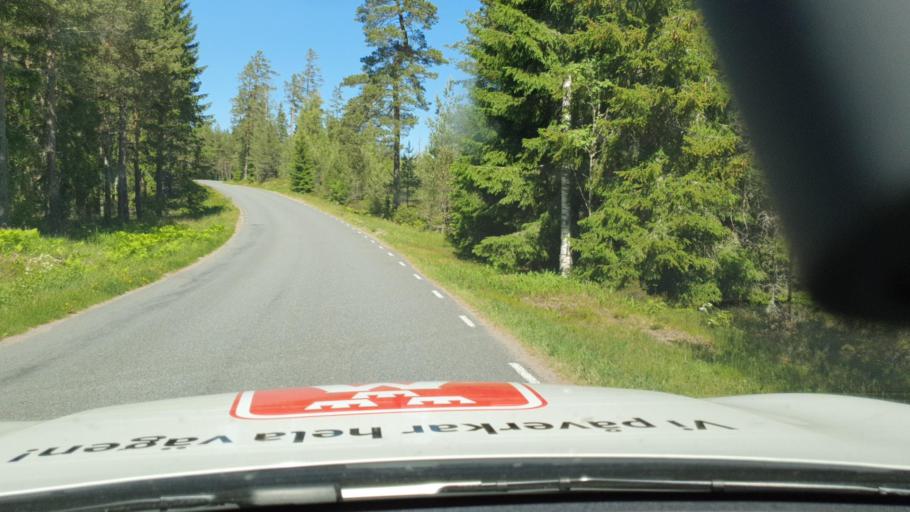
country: SE
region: Joenkoeping
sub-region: Habo Kommun
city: Habo
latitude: 57.9933
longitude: 14.0068
